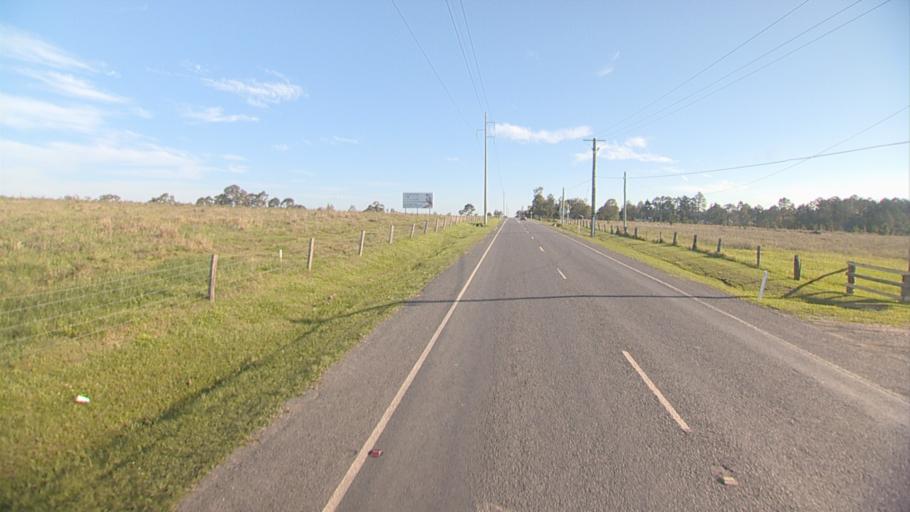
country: AU
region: Queensland
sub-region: Logan
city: Waterford West
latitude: -27.7049
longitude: 153.1173
